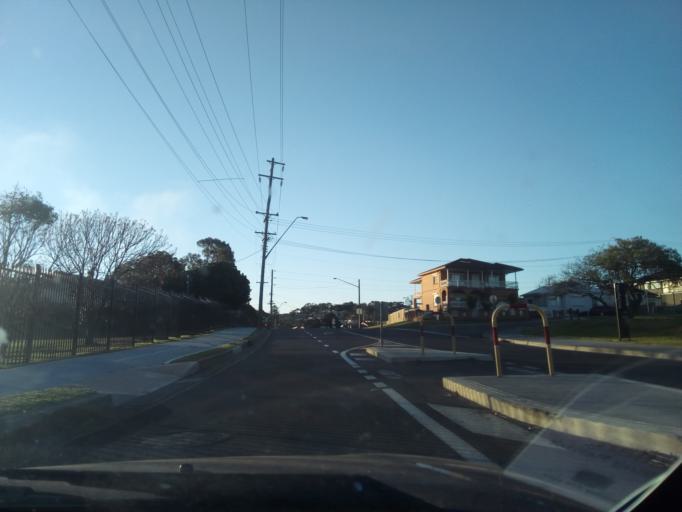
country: AU
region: New South Wales
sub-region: Wollongong
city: Port Kembla
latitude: -34.4900
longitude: 150.8944
